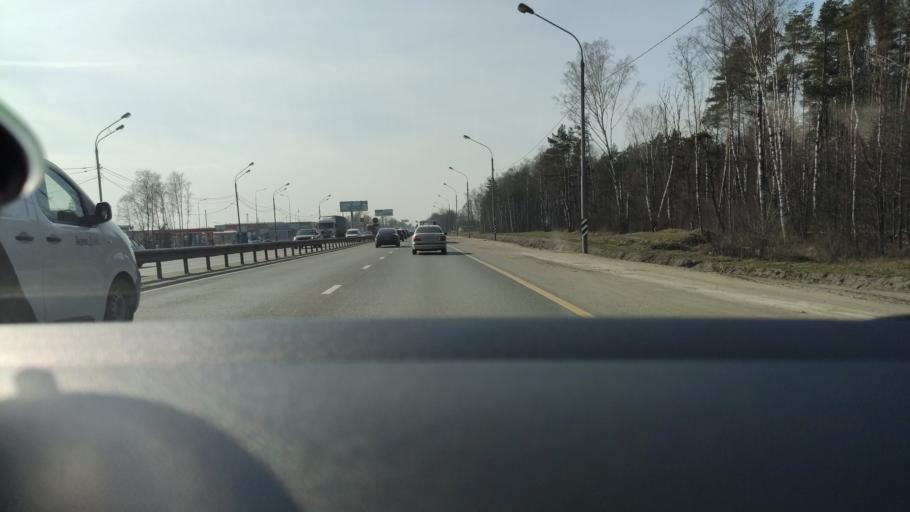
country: RU
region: Moskovskaya
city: Staraya Kupavna
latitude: 55.8217
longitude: 38.1794
